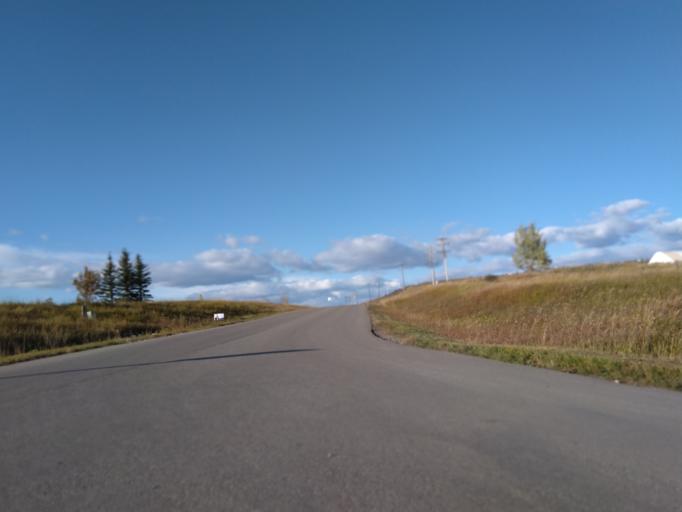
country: CA
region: Alberta
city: Cochrane
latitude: 51.1738
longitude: -114.4670
